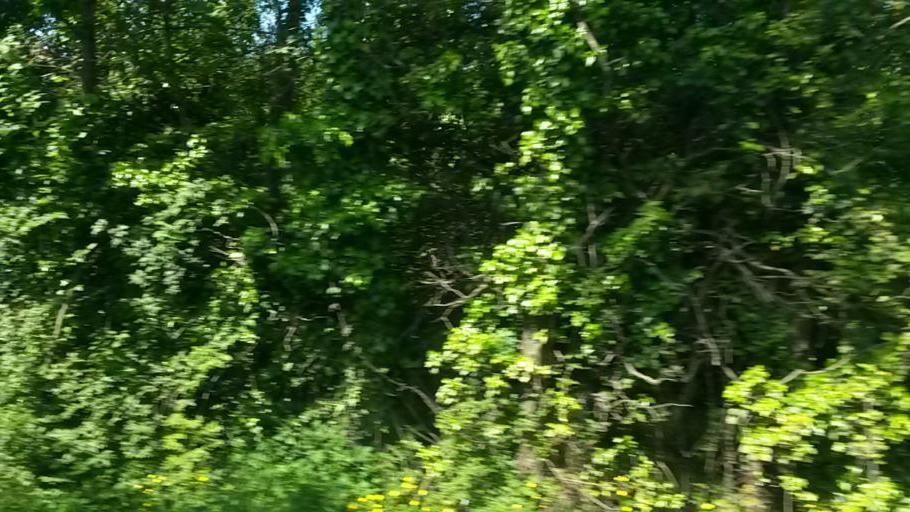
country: IE
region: Leinster
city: Donabate
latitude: 53.4922
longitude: -6.1816
